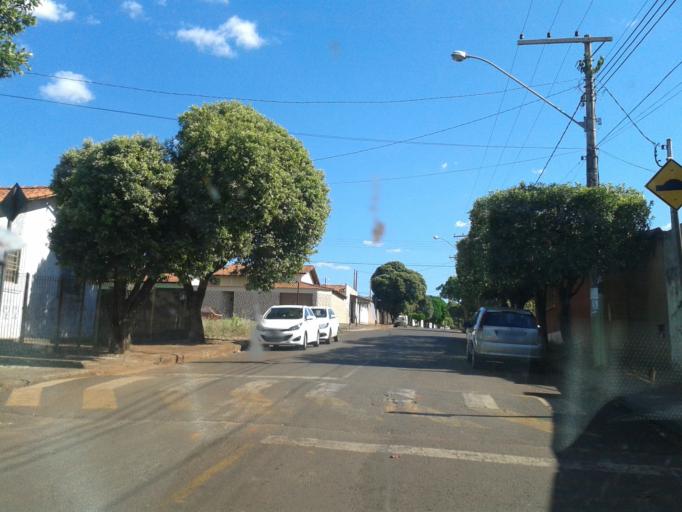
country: BR
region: Minas Gerais
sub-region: Ituiutaba
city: Ituiutaba
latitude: -18.9509
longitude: -49.4601
